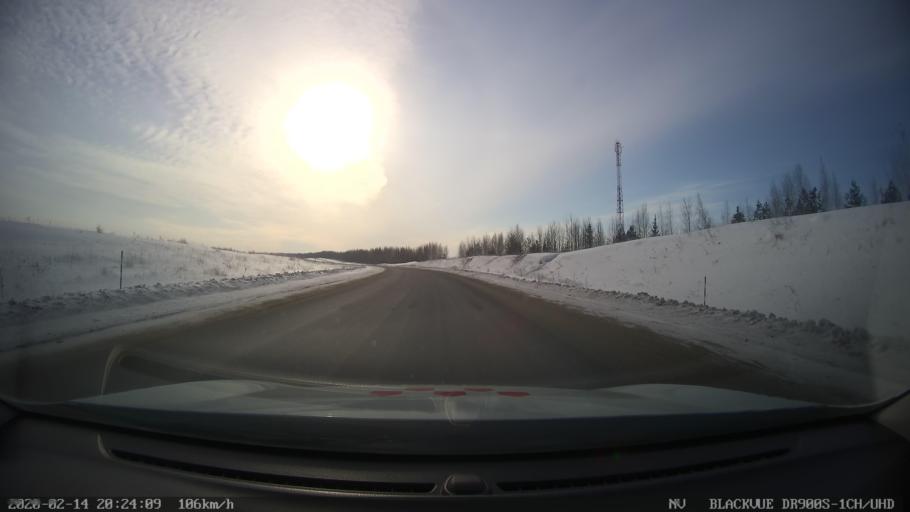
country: RU
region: Tatarstan
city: Verkhniy Uslon
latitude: 55.5169
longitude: 48.9671
